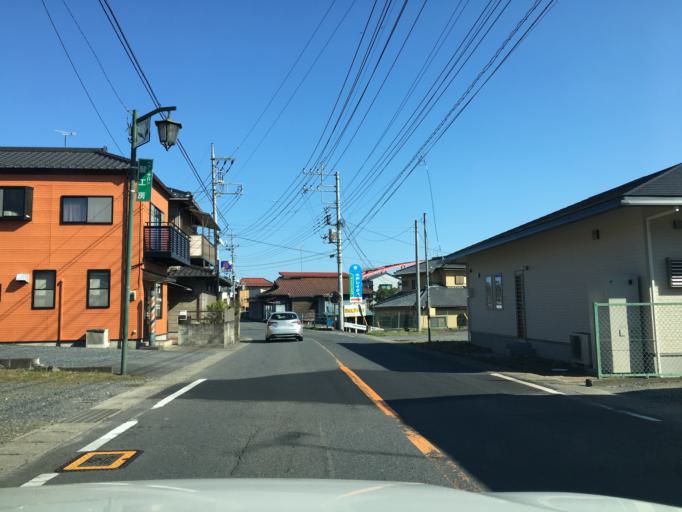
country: JP
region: Ibaraki
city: Omiya
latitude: 36.5487
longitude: 140.3304
